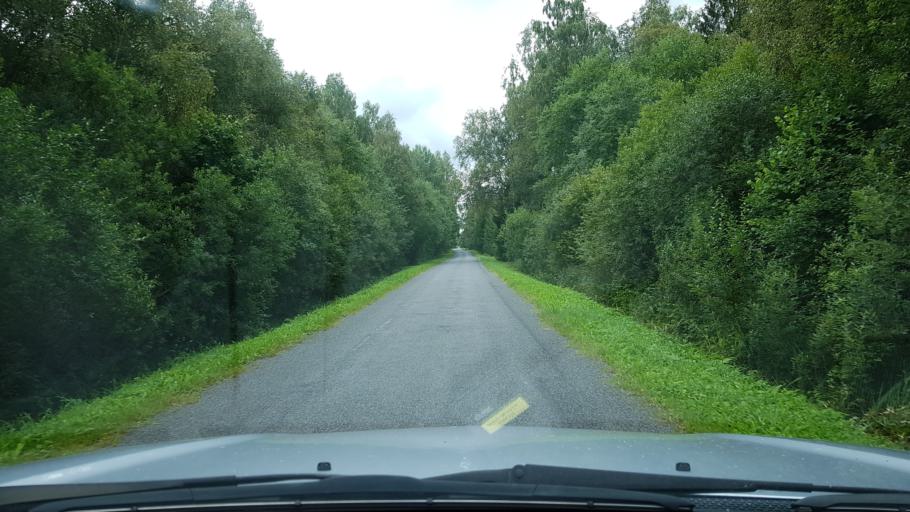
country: EE
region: Harju
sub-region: Rae vald
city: Vaida
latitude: 59.2981
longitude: 24.9966
